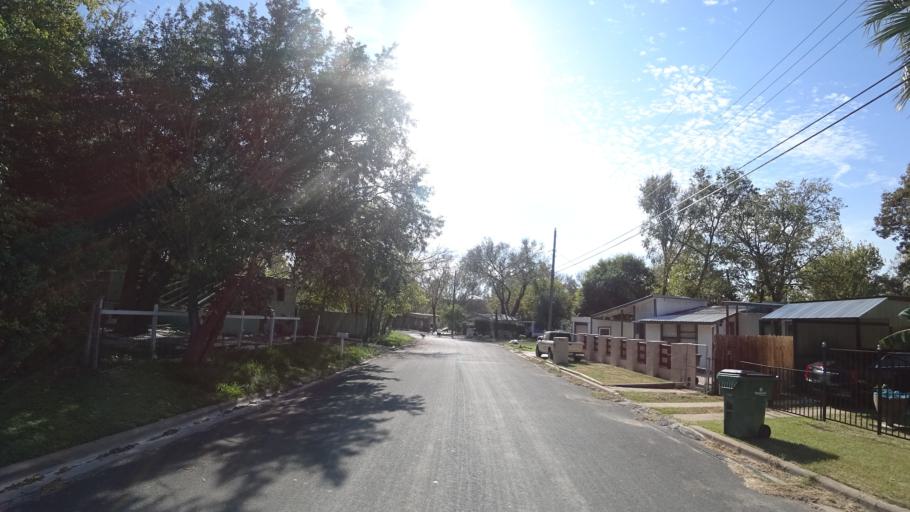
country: US
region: Texas
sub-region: Travis County
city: Pflugerville
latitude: 30.4053
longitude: -97.6341
